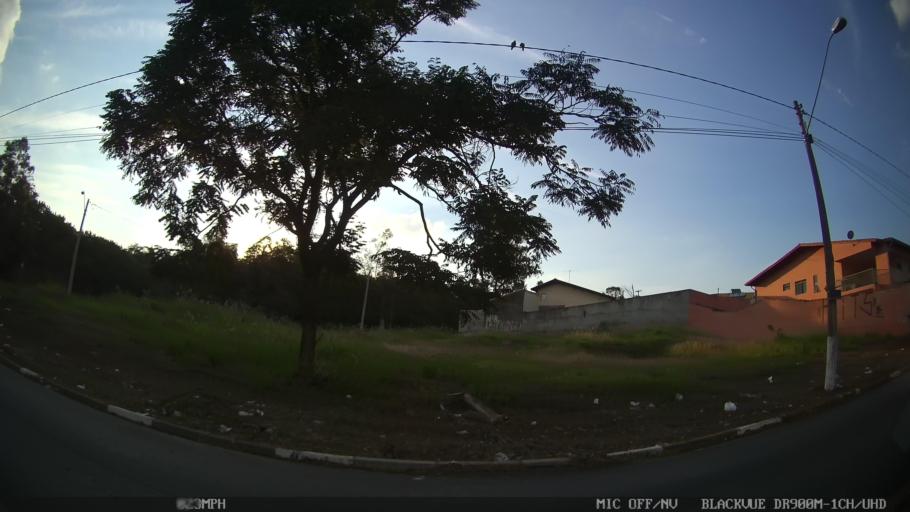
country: BR
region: Sao Paulo
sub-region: Hortolandia
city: Hortolandia
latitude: -22.8916
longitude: -47.1505
